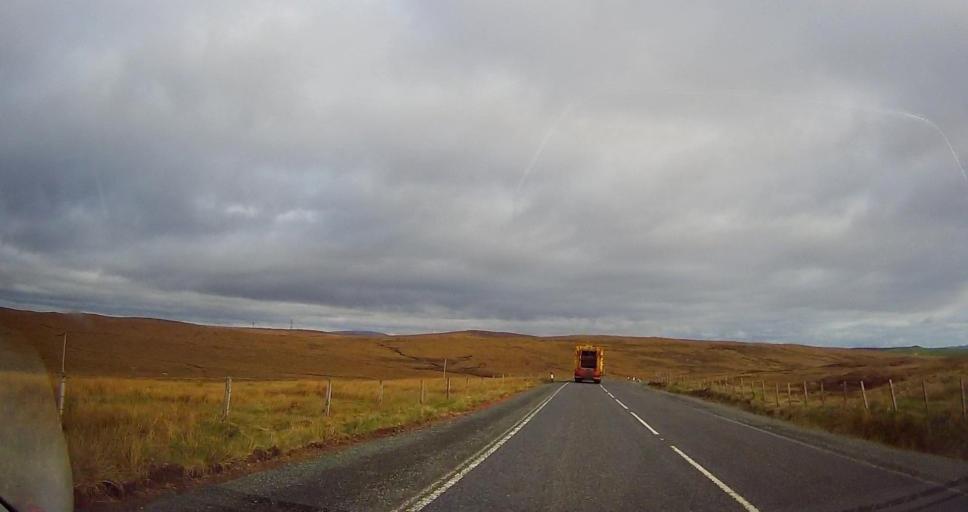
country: GB
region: Scotland
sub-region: Shetland Islands
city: Lerwick
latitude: 60.4486
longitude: -1.2113
